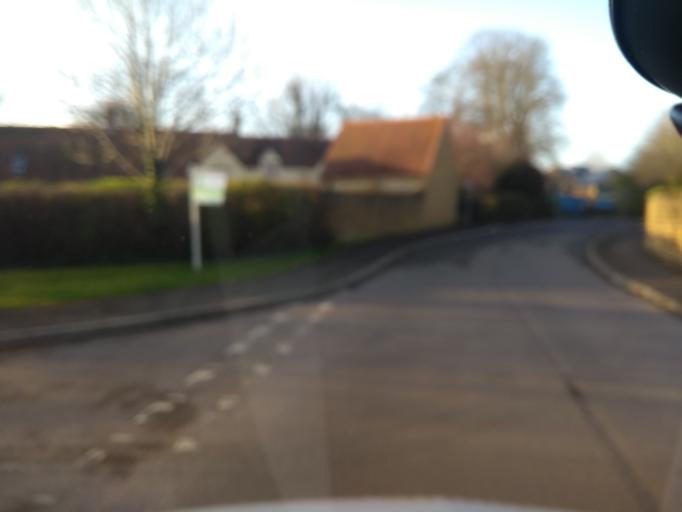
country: GB
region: England
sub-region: Somerset
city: Stoke-sub-Hamdon
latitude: 50.9559
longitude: -2.7522
